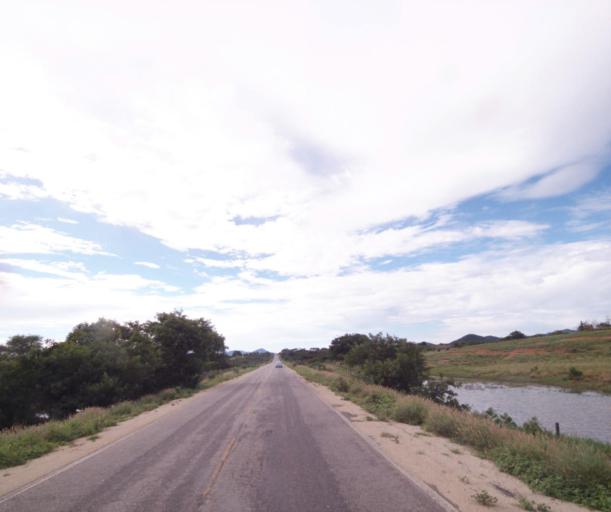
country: BR
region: Bahia
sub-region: Guanambi
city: Guanambi
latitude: -14.4107
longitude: -42.7395
